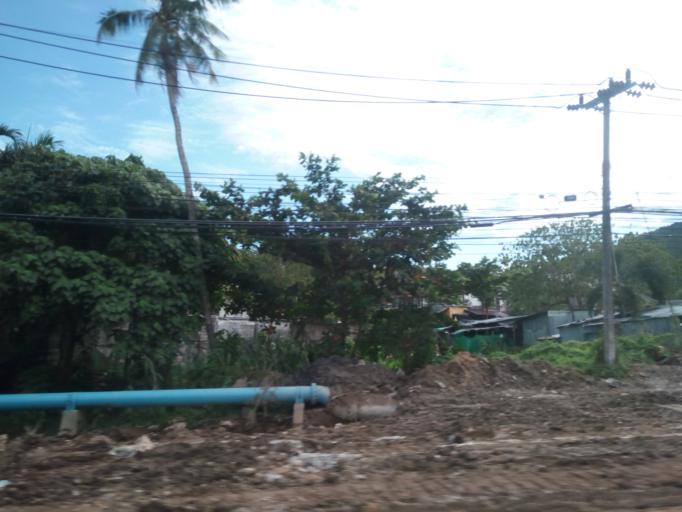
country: TH
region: Phuket
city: Mueang Phuket
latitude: 7.8342
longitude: 98.3982
